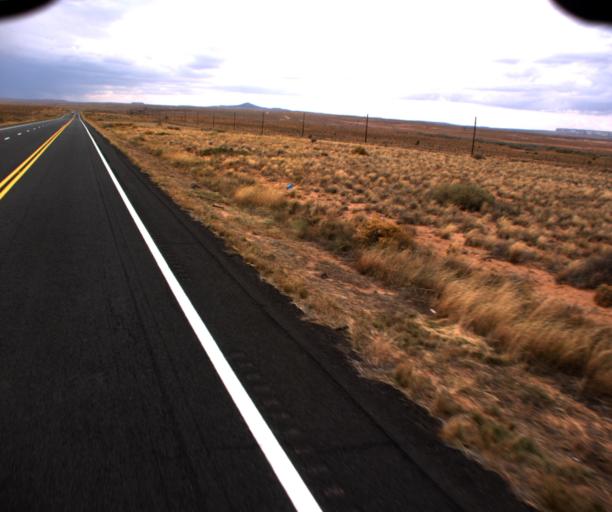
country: US
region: Arizona
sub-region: Coconino County
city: Kaibito
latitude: 36.3999
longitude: -110.8573
